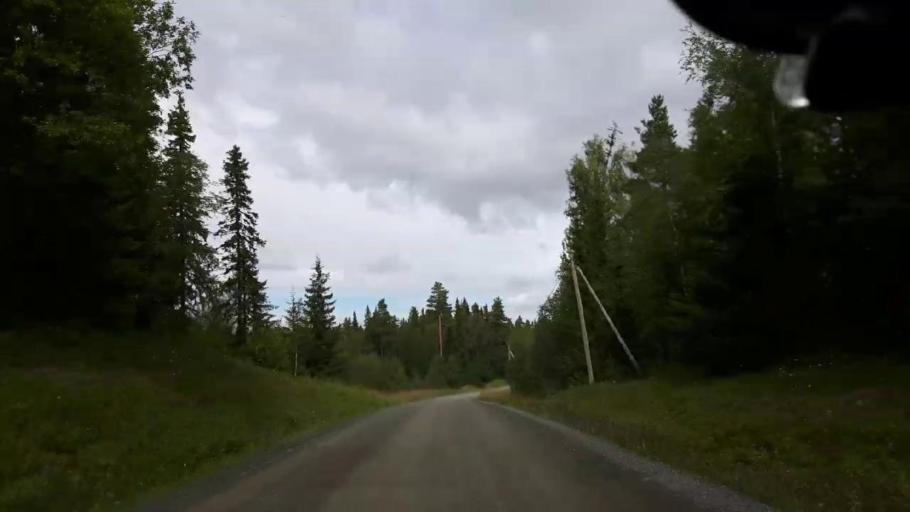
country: SE
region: Jaemtland
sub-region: Krokoms Kommun
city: Valla
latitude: 63.4014
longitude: 14.0950
